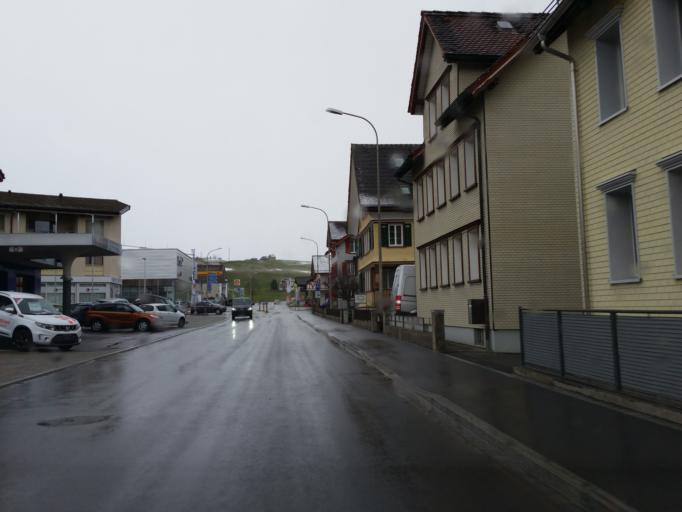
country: CH
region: Appenzell Innerrhoden
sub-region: Appenzell Inner Rhodes
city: Appenzell
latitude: 47.3319
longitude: 9.3983
